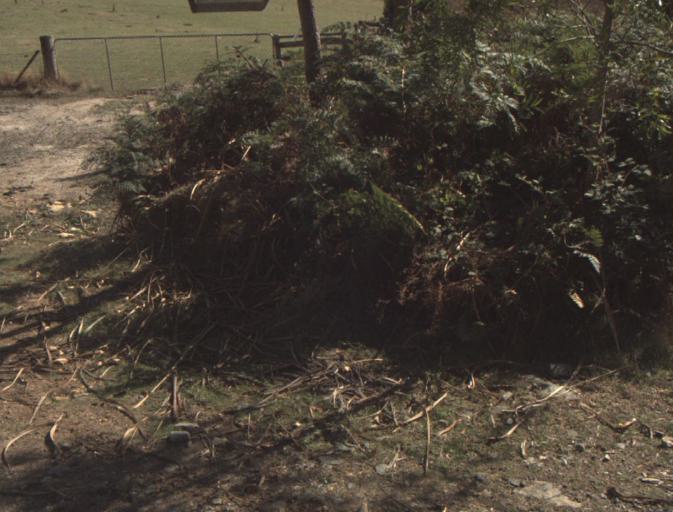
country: AU
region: Tasmania
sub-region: Launceston
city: Mayfield
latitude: -41.2172
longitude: 147.2401
